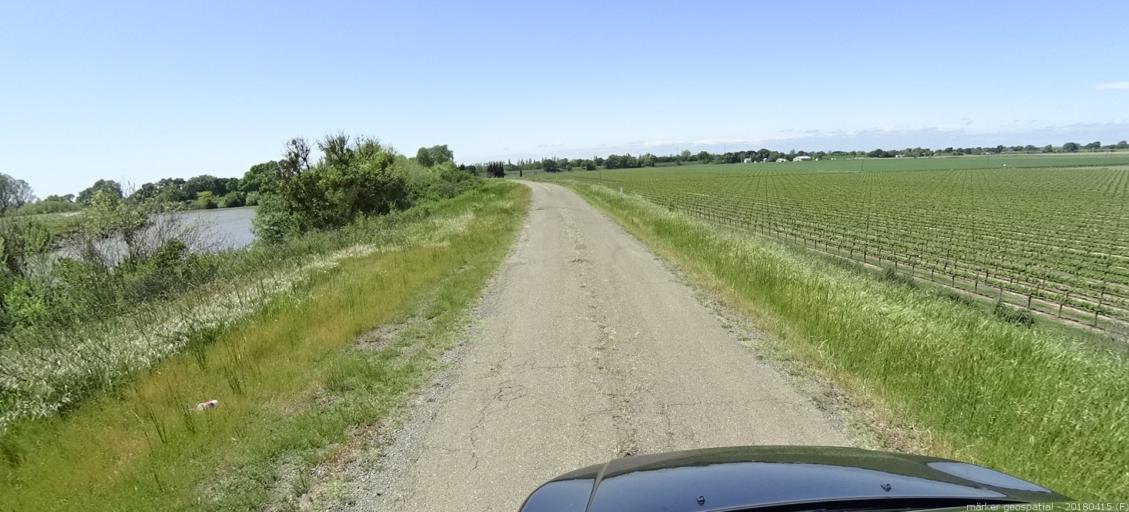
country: US
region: California
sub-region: Sacramento County
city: Walnut Grove
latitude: 38.2628
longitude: -121.5915
